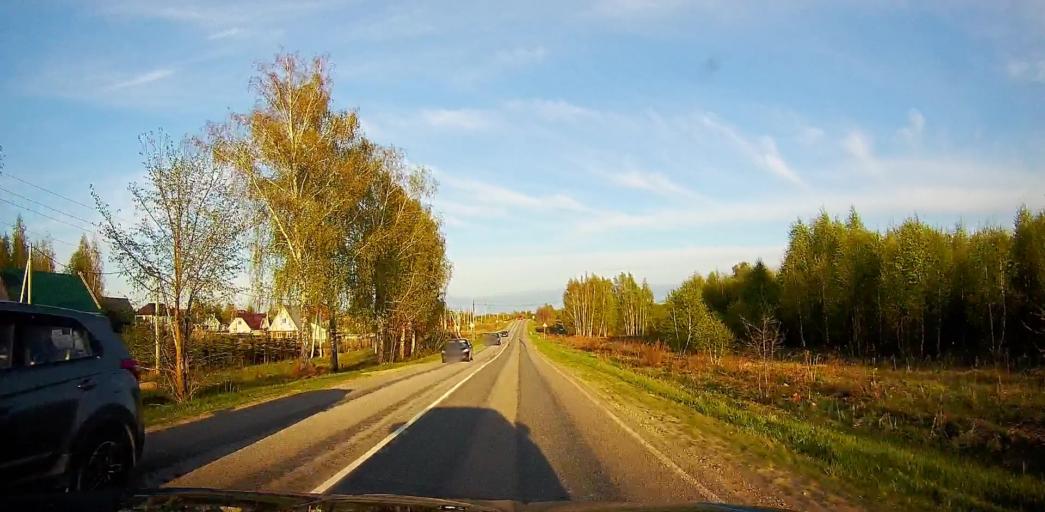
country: RU
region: Moskovskaya
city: Meshcherino
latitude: 55.2500
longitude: 38.2883
